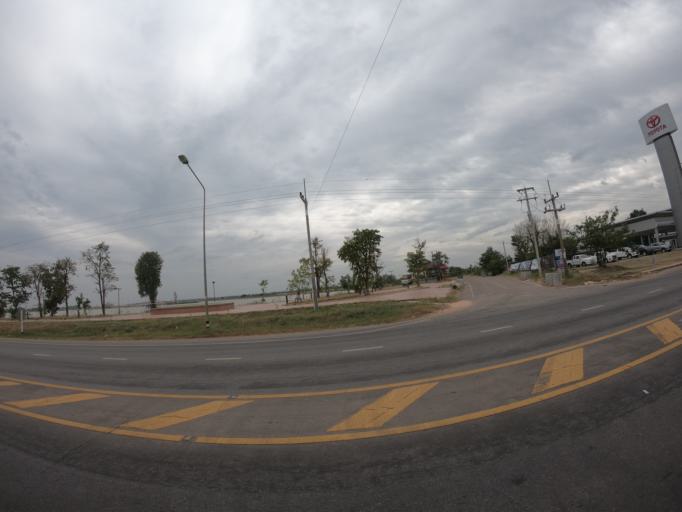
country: TH
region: Roi Et
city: Thawat Buri
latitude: 16.0827
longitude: 103.7168
